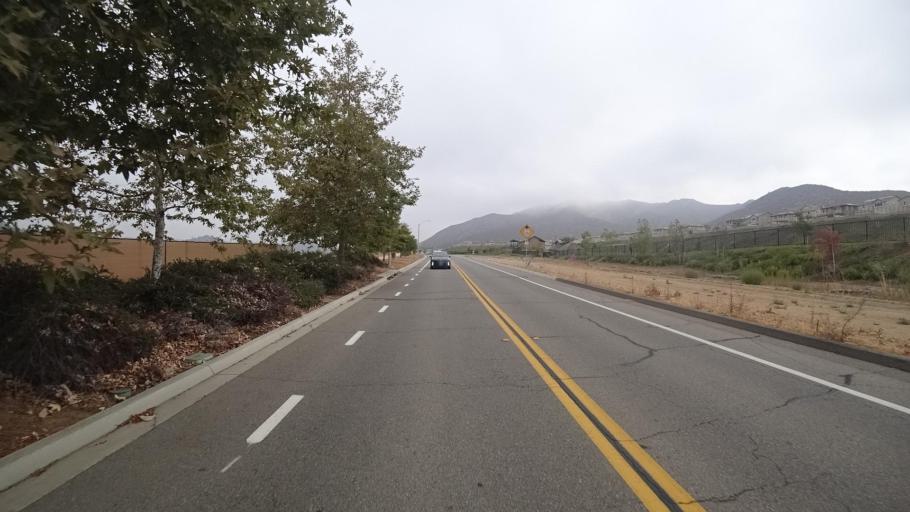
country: US
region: California
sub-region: San Diego County
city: Rainbow
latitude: 33.3545
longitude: -117.1555
